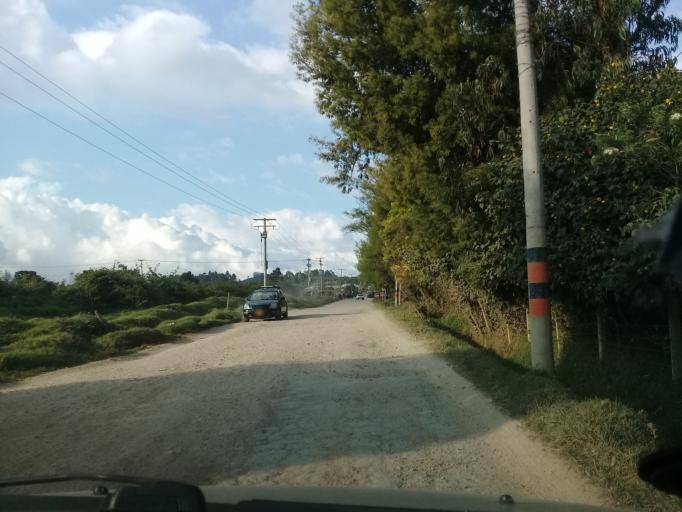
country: CO
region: Cundinamarca
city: Madrid
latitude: 4.7866
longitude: -74.2203
